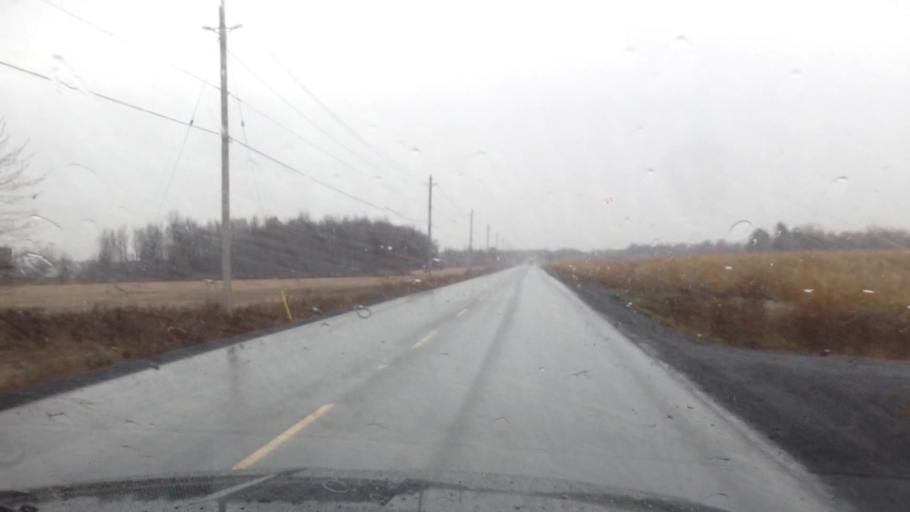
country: CA
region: Ontario
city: Bourget
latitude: 45.3010
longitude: -75.2482
